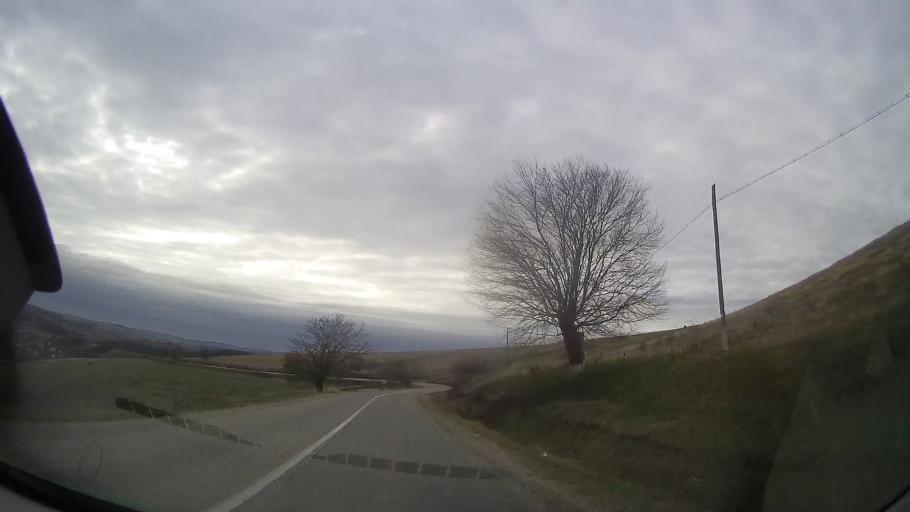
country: RO
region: Bistrita-Nasaud
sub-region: Comuna Budesti
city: Budesti
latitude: 46.8873
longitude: 24.2405
